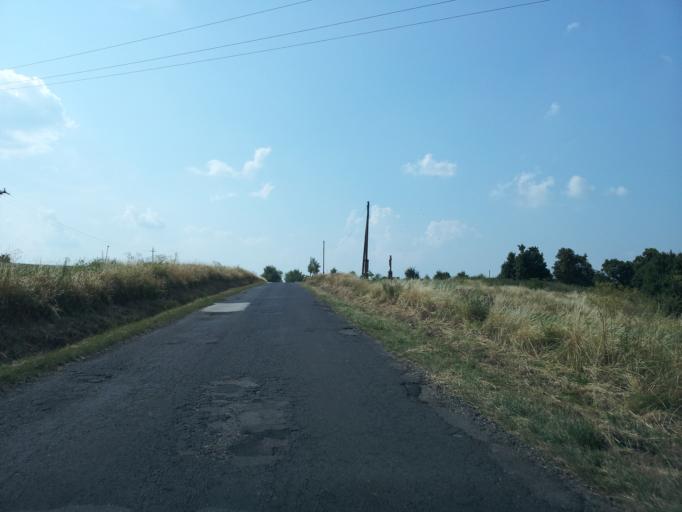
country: HU
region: Veszprem
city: Balatonfured
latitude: 47.0091
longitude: 17.8208
